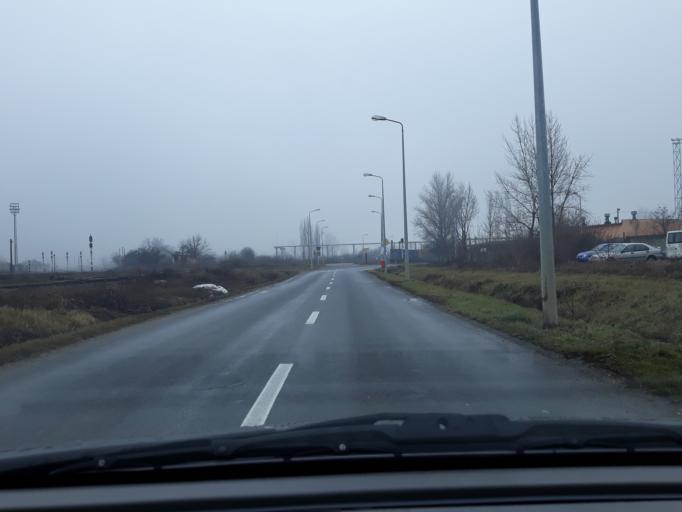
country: RO
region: Bihor
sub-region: Comuna Sanmartin
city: Sanmartin
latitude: 47.0379
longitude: 21.9656
